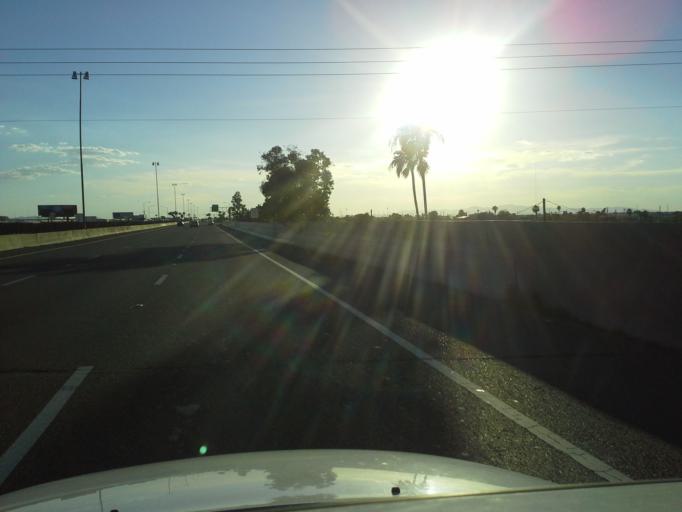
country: US
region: Arizona
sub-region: Maricopa County
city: Phoenix
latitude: 33.4298
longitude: -112.0907
